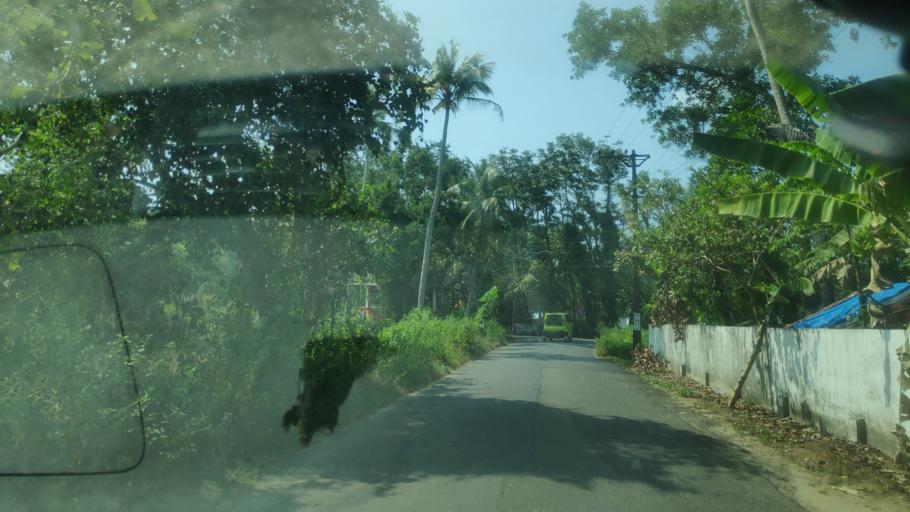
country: IN
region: Kerala
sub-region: Alappuzha
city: Vayalar
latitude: 9.6631
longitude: 76.3052
